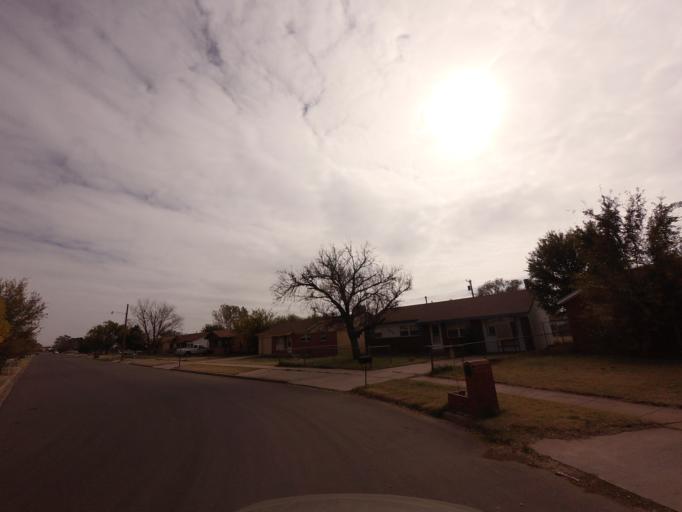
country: US
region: New Mexico
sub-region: Curry County
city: Clovis
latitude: 34.4299
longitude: -103.2224
